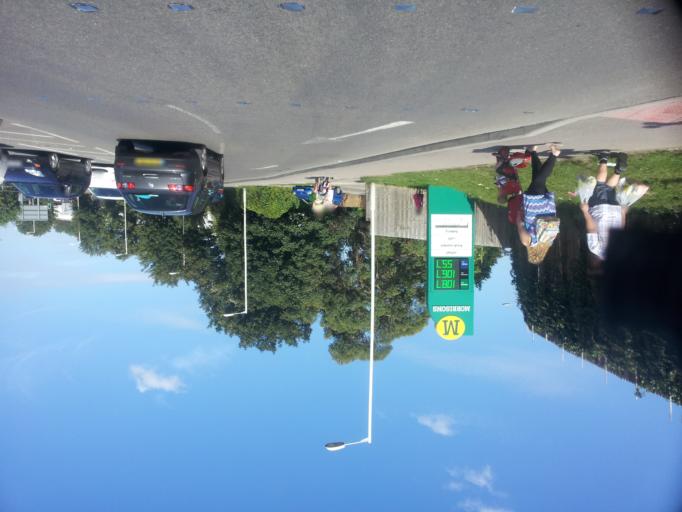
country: GB
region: England
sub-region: Kent
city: Sittingbourne
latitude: 51.3444
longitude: 0.7322
